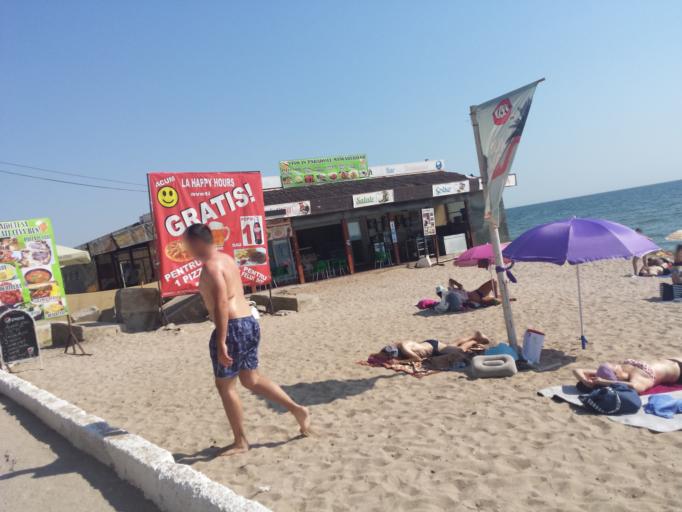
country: RO
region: Constanta
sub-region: Comuna Douazeci si Trei August
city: Douazeci si Trei August
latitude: 43.8614
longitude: 28.6060
